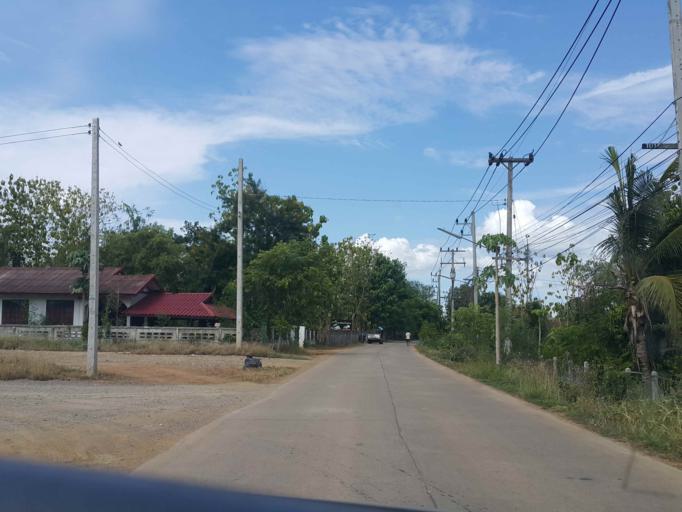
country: TH
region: Sukhothai
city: Thung Saliam
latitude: 17.3289
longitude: 99.5640
